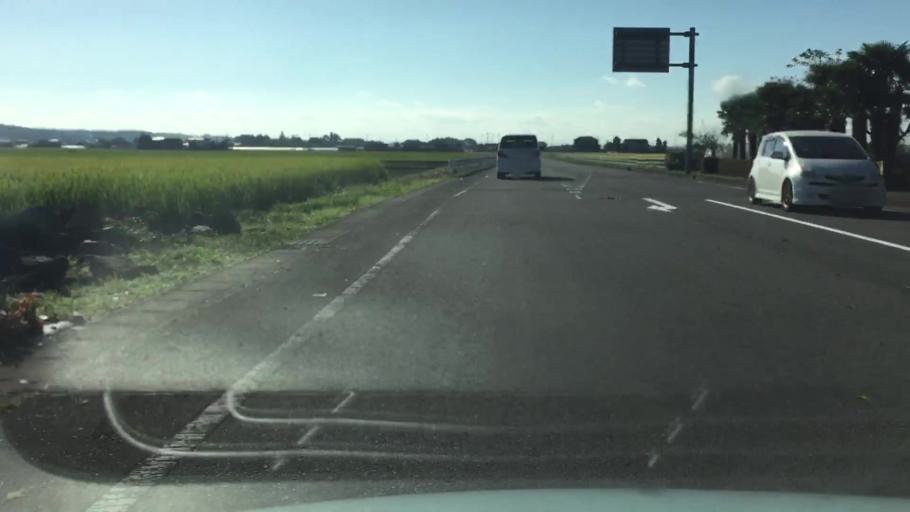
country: JP
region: Tochigi
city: Ujiie
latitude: 36.6757
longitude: 140.0134
